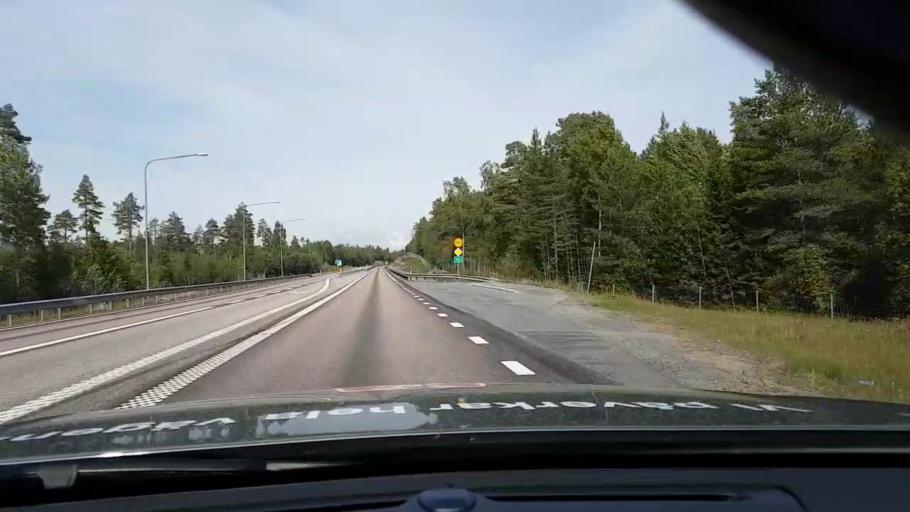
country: SE
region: Vaesternorrland
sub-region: OErnskoeldsviks Kommun
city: Husum
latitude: 63.3750
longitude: 19.1903
